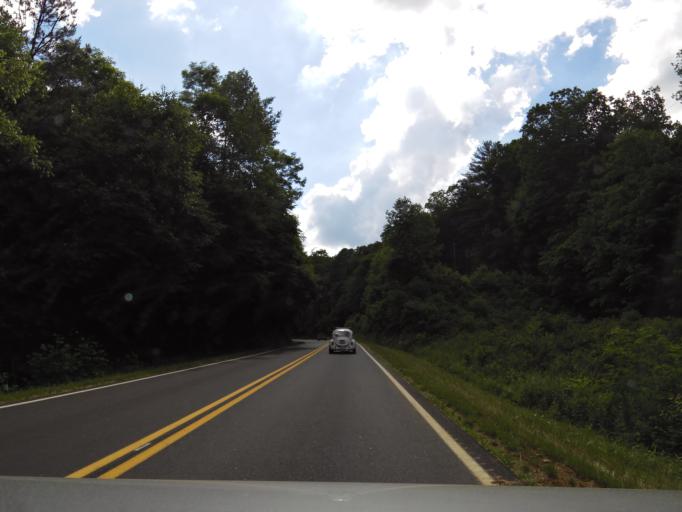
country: US
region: Georgia
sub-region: Towns County
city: Hiawassee
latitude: 34.8562
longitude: -83.7865
